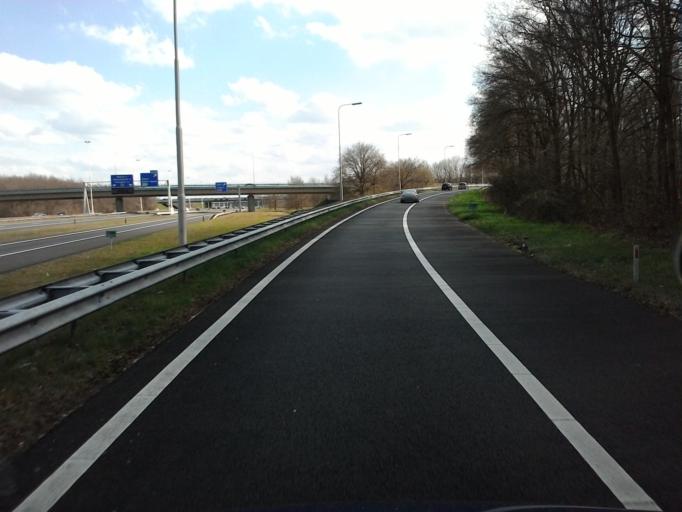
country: NL
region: North Holland
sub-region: Gemeente Laren
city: Laren
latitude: 52.2348
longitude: 5.2342
